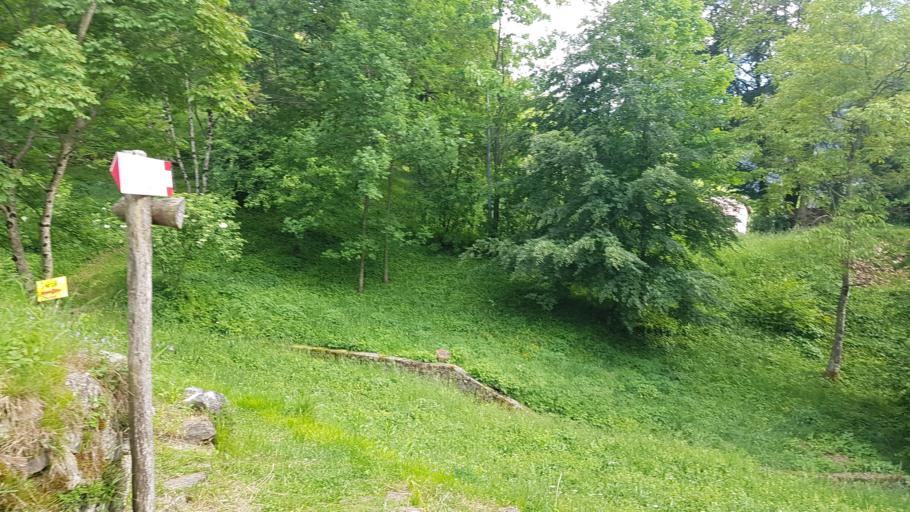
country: IT
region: Friuli Venezia Giulia
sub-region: Provincia di Udine
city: Moggio Udinese
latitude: 46.4688
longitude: 13.1943
